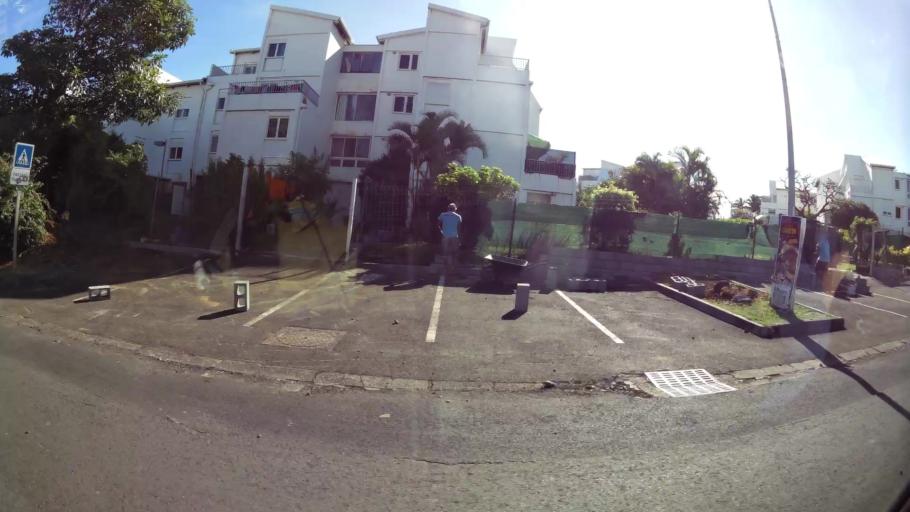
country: RE
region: Reunion
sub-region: Reunion
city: Saint-Pierre
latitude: -21.3457
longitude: 55.4916
